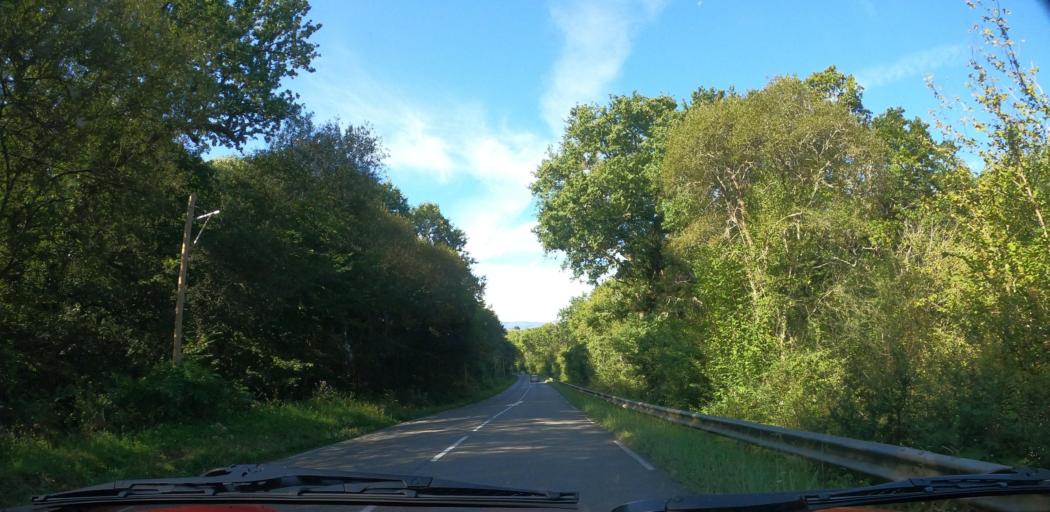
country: FR
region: Aquitaine
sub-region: Departement des Pyrenees-Atlantiques
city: Saint-Pee-sur-Nivelle
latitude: 43.3785
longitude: -1.5401
